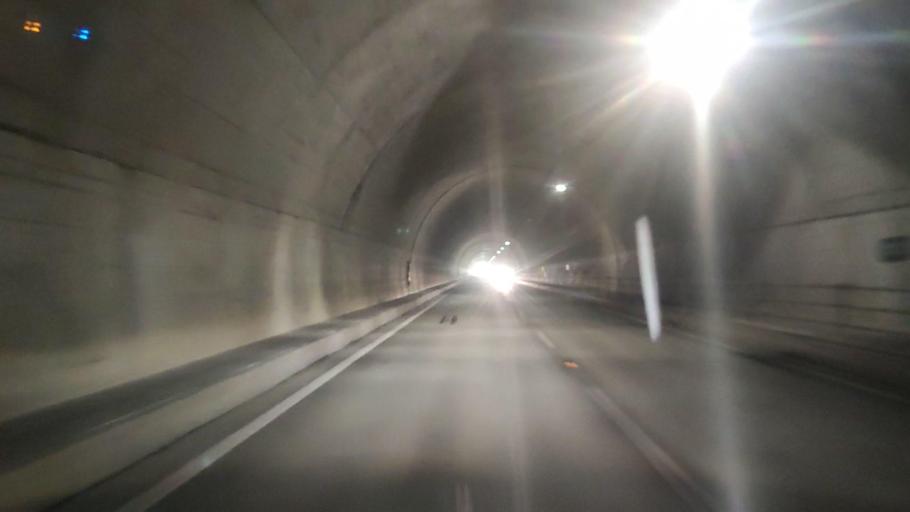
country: JP
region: Miyazaki
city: Nobeoka
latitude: 32.7340
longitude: 131.8253
